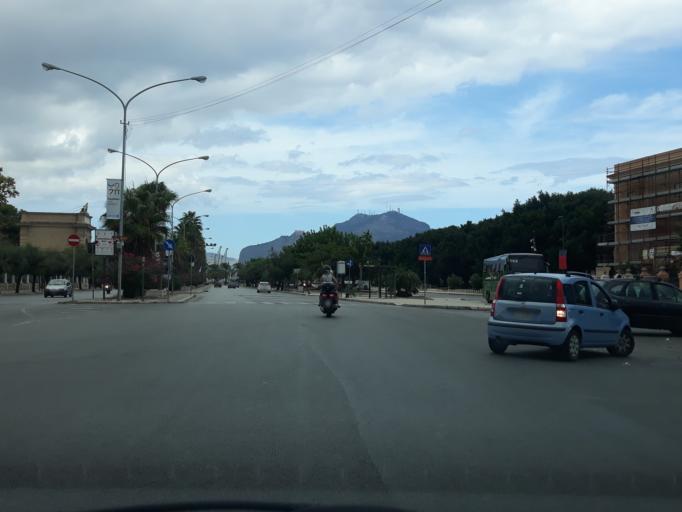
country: IT
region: Sicily
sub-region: Palermo
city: Palermo
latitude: 38.1129
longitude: 13.3780
